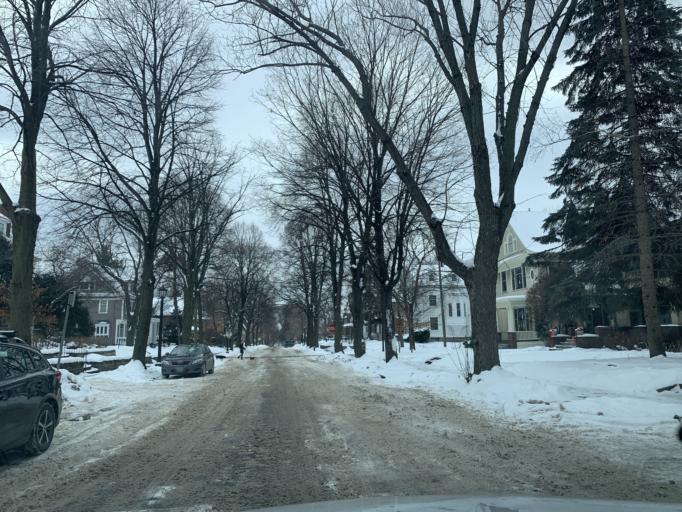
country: US
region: Minnesota
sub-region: Hennepin County
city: Minneapolis
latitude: 44.9660
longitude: -93.2982
